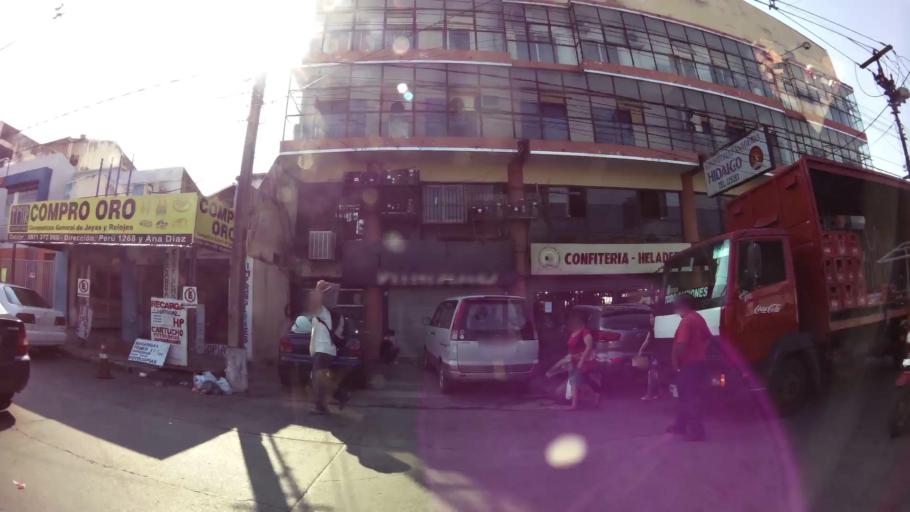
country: PY
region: Asuncion
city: Asuncion
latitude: -25.2990
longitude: -57.6263
